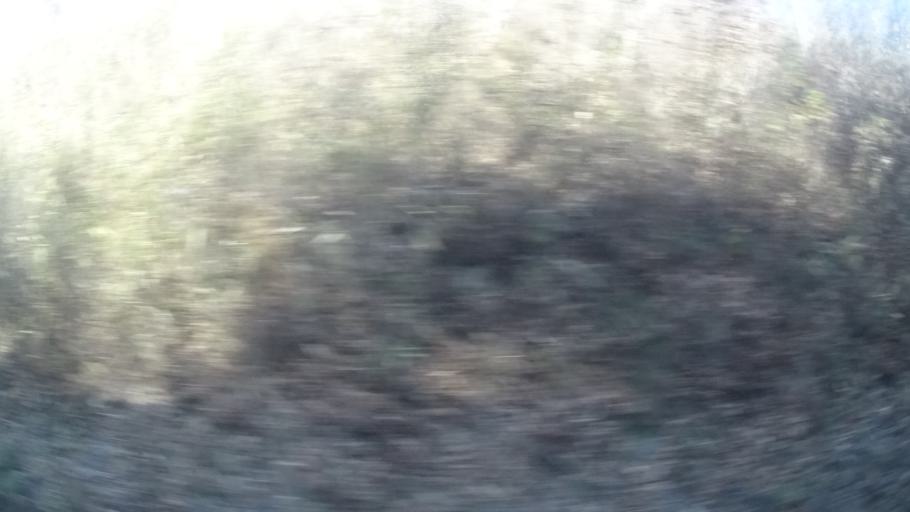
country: JP
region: Miyagi
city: Marumori
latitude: 37.7493
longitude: 140.9392
